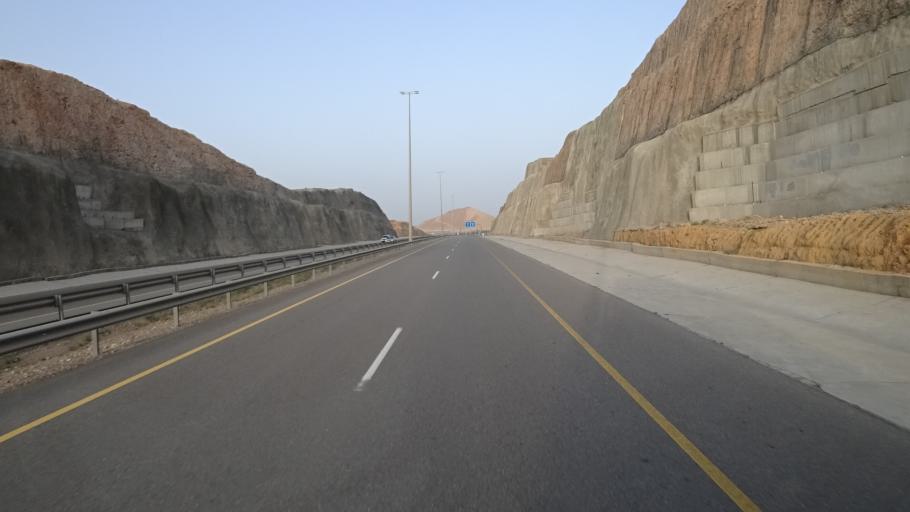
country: OM
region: Muhafazat Masqat
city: Muscat
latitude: 23.2055
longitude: 58.9074
